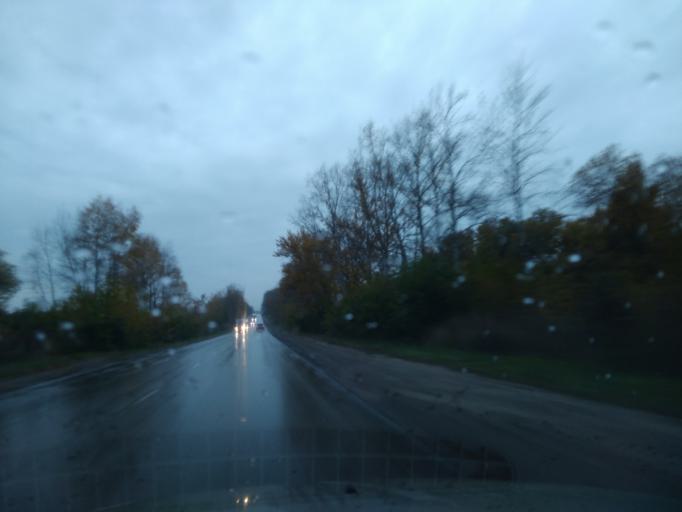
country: RU
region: Tula
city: Yefremov
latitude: 53.1535
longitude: 38.0520
